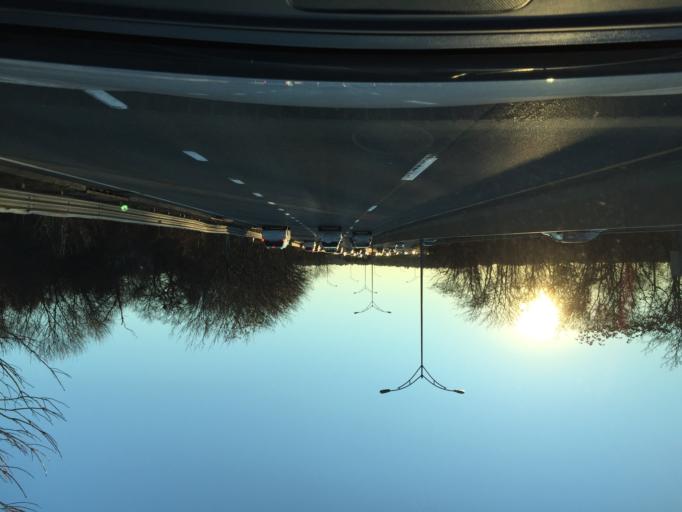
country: US
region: Massachusetts
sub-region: Middlesex County
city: Waltham
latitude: 42.3426
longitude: -71.2572
